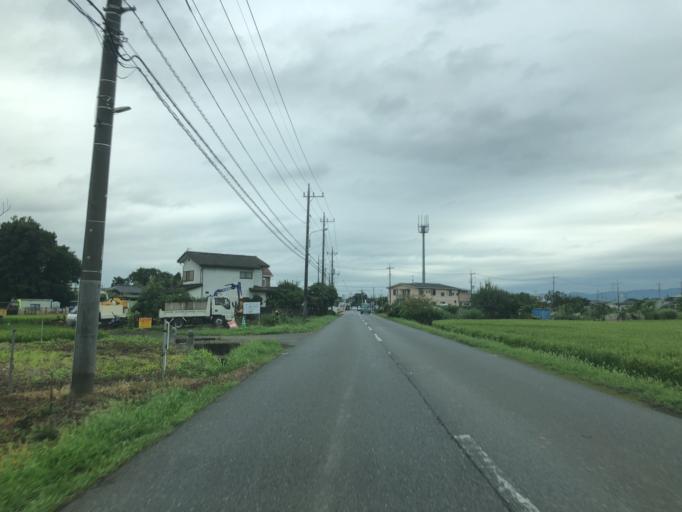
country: JP
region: Saitama
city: Sakado
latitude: 35.9821
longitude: 139.3976
